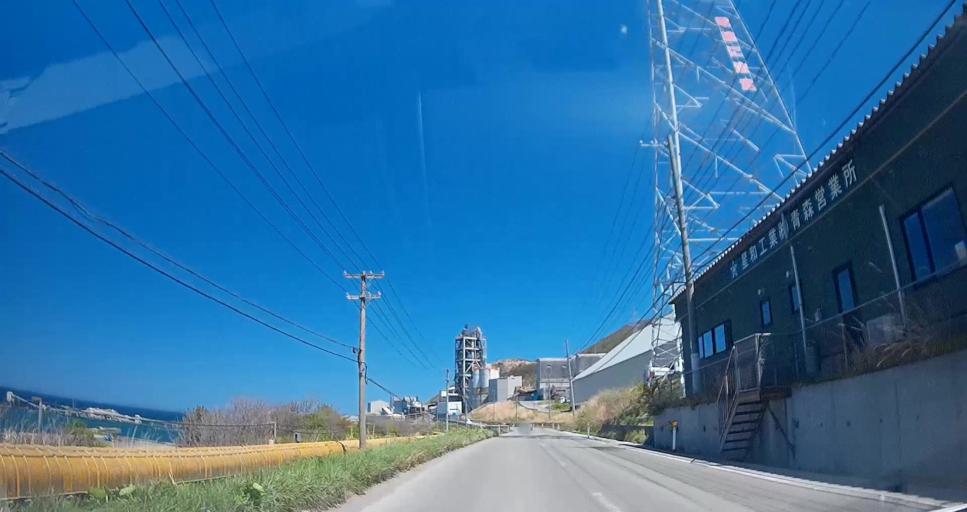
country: JP
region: Aomori
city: Mutsu
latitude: 41.4041
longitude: 141.4316
